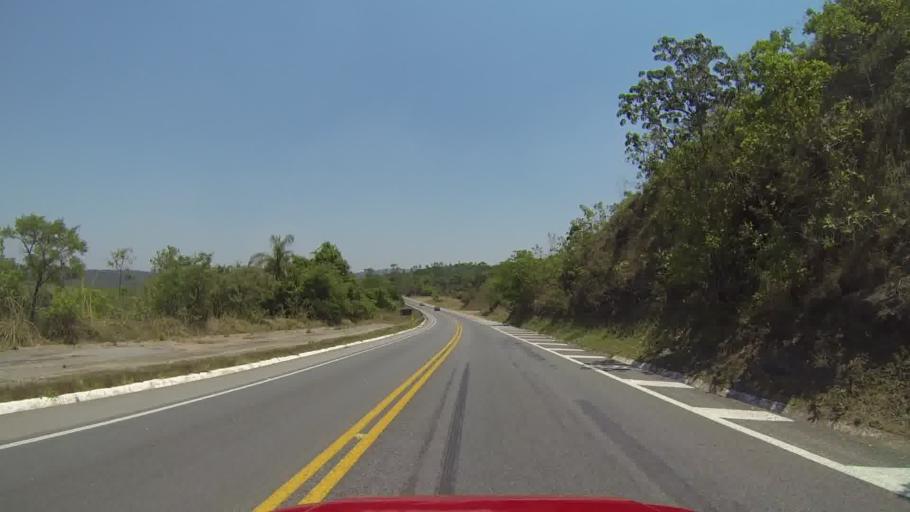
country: BR
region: Minas Gerais
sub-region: Itapecerica
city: Itapecerica
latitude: -20.2806
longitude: -45.1331
